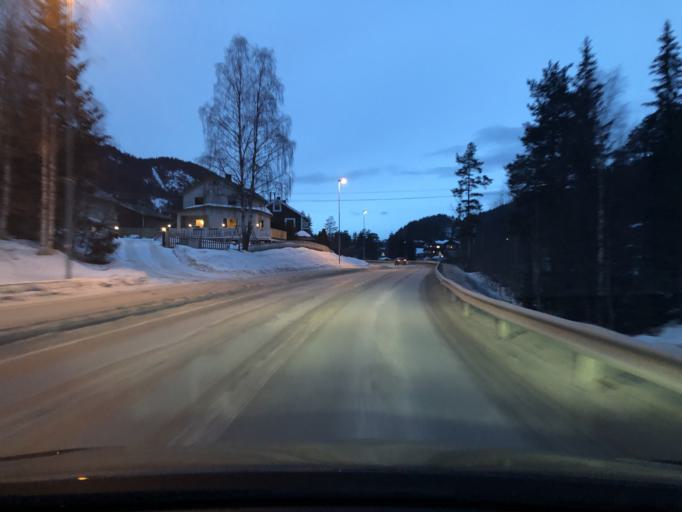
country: NO
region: Oppland
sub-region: Nord-Aurdal
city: Fagernes
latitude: 60.9885
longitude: 9.2254
